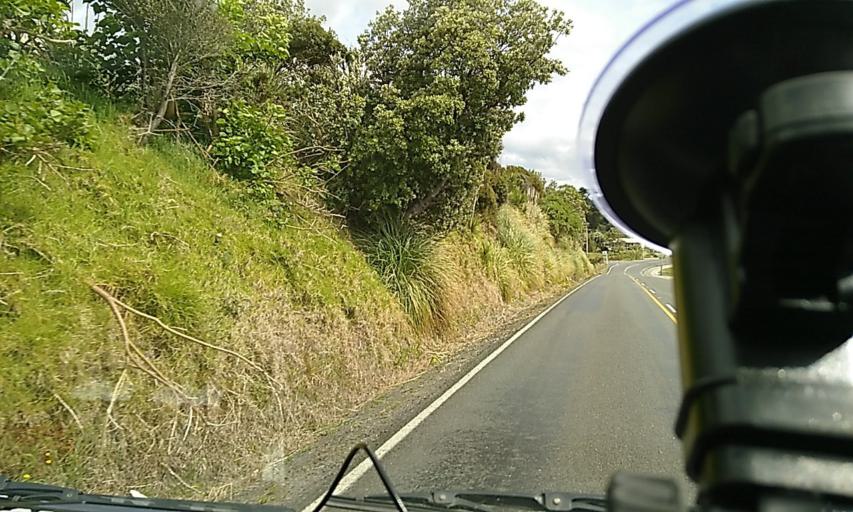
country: NZ
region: Northland
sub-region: Far North District
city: Ahipara
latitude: -35.5147
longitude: 173.3890
